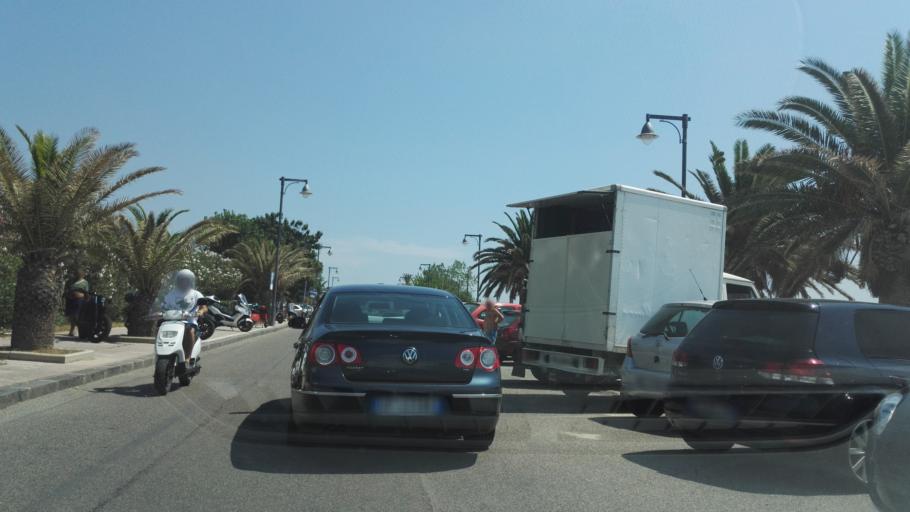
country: IT
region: Calabria
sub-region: Provincia di Reggio Calabria
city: Roccella Ionica
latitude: 38.3225
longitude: 16.4105
